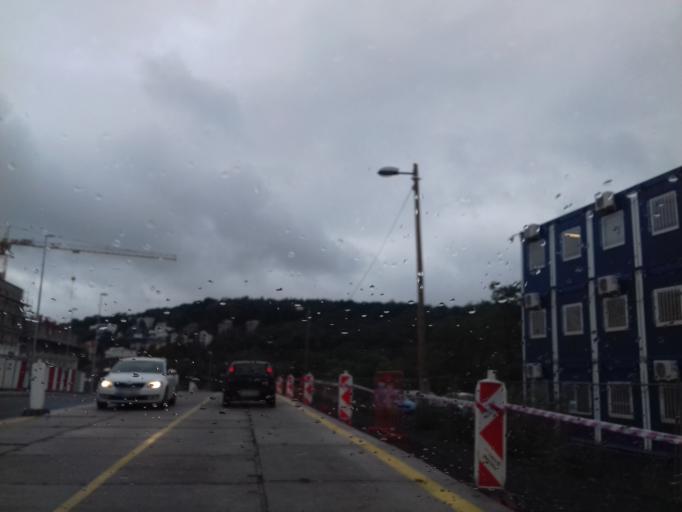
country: CZ
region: Praha
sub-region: Praha 1
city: Mala Strana
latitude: 50.0586
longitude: 14.3755
